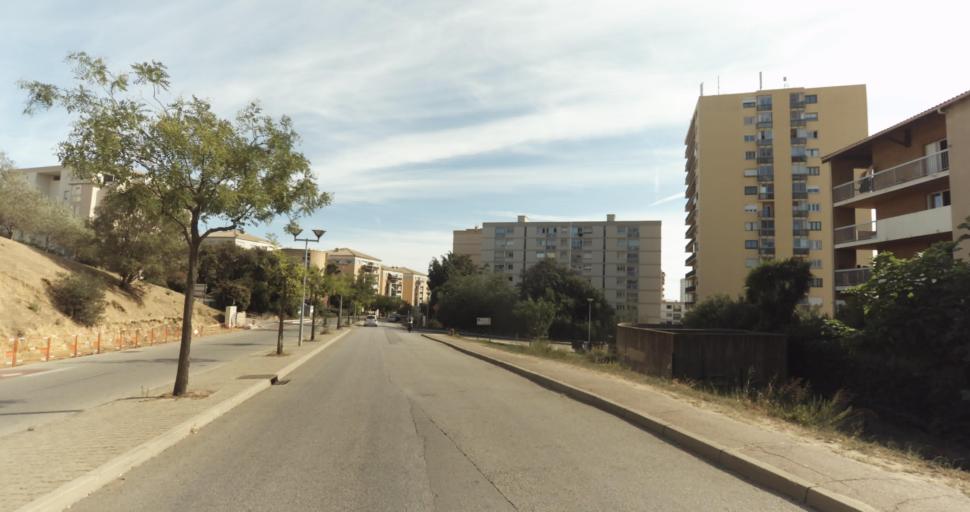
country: FR
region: Corsica
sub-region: Departement de la Corse-du-Sud
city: Ajaccio
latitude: 41.9411
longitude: 8.7500
